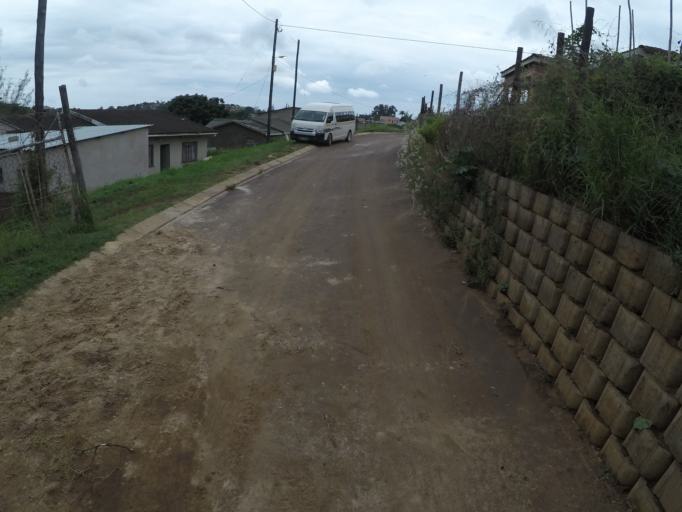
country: ZA
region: KwaZulu-Natal
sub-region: uThungulu District Municipality
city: Empangeni
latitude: -28.7811
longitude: 31.8613
